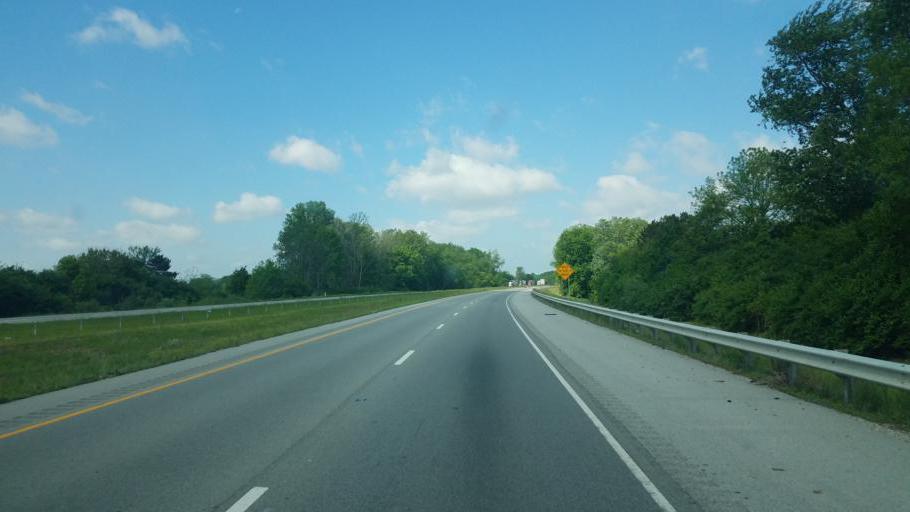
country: US
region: Indiana
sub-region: Putnam County
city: Cloverdale
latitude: 39.5625
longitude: -86.6475
